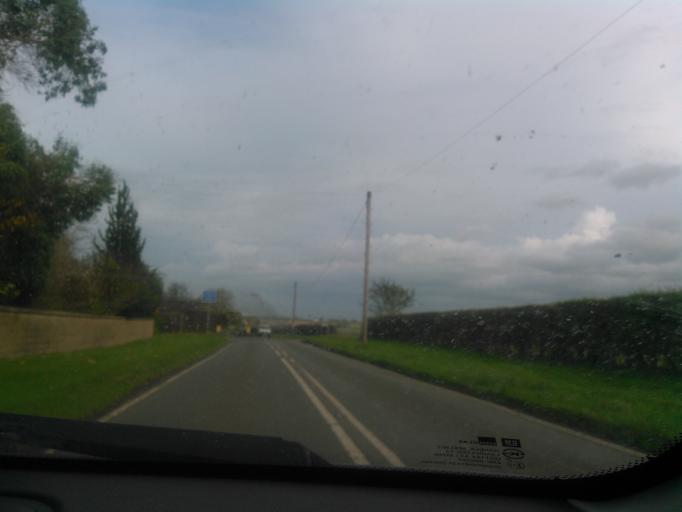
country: GB
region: England
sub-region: Shropshire
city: Clive
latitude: 52.8094
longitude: -2.7492
